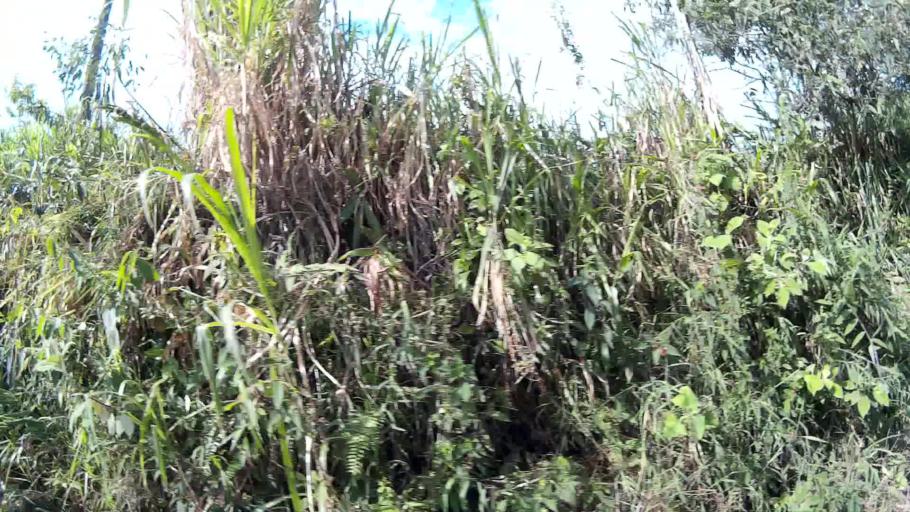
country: CO
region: Quindio
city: Filandia
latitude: 4.6882
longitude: -75.6691
